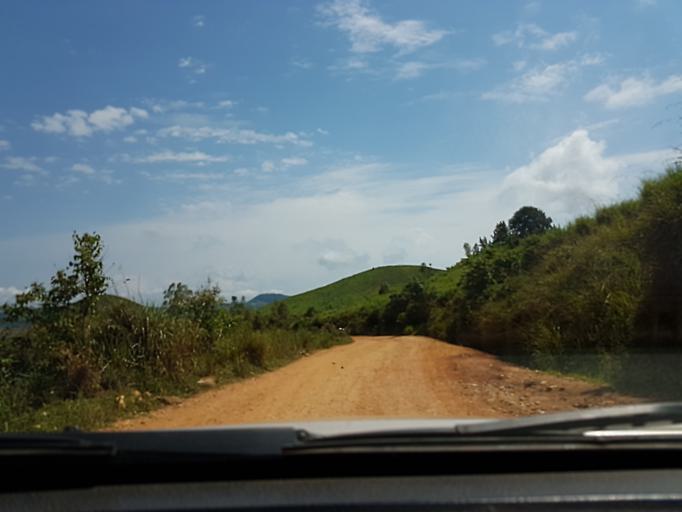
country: RW
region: Western Province
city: Cyangugu
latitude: -2.7024
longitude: 28.9155
